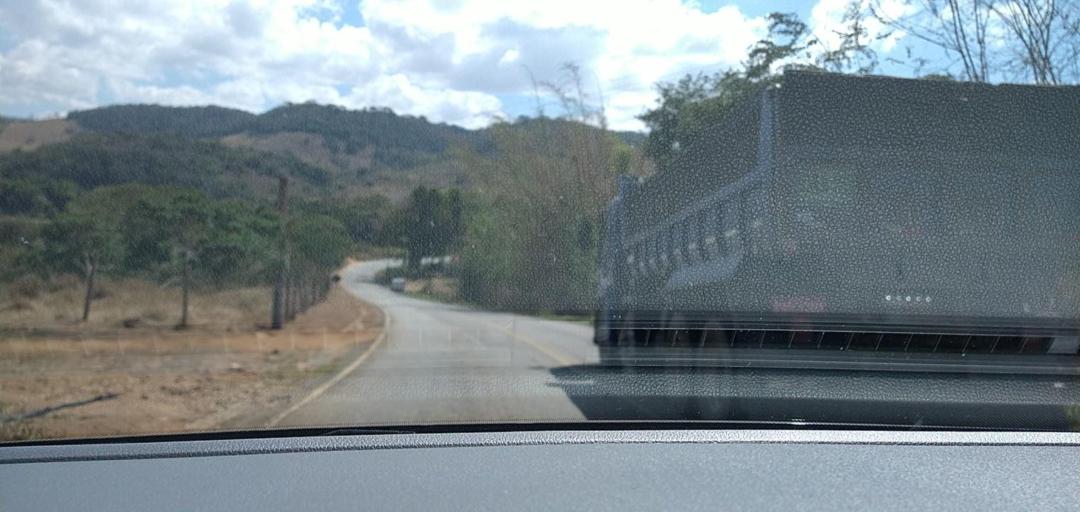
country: BR
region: Minas Gerais
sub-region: Ponte Nova
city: Ponte Nova
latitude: -20.2816
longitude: -42.9022
